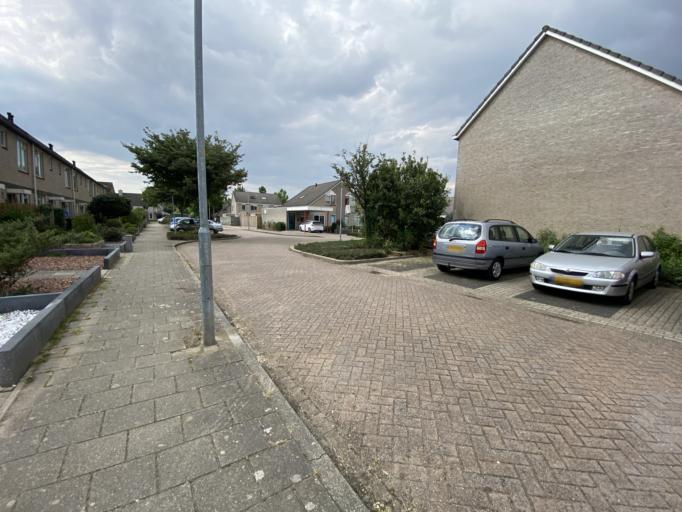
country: NL
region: Gelderland
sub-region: Gemeente Duiven
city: Duiven
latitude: 51.9454
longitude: 5.9981
